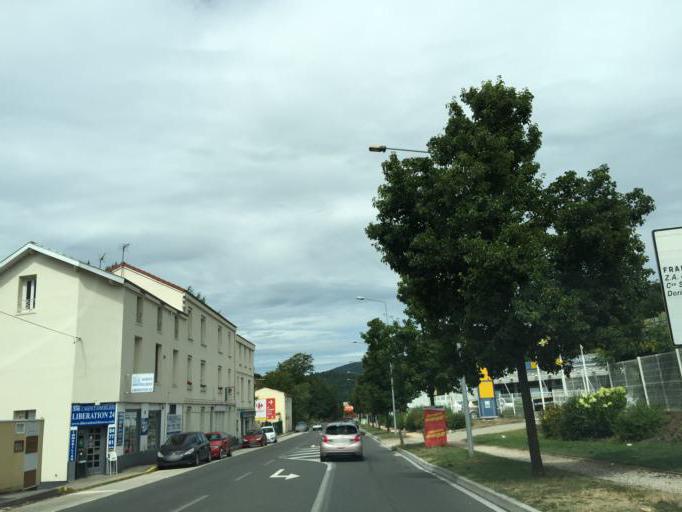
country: FR
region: Rhone-Alpes
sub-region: Departement de la Loire
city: Unieux
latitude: 45.3912
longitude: 4.2754
